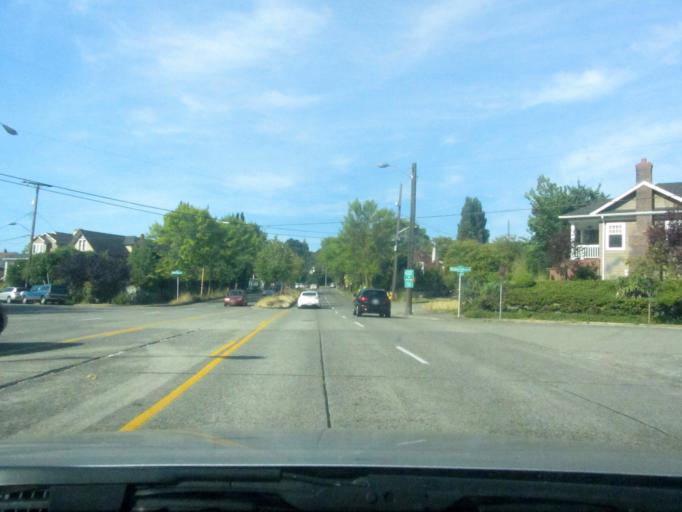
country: US
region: Washington
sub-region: King County
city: Seattle
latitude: 47.6631
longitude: -122.3444
